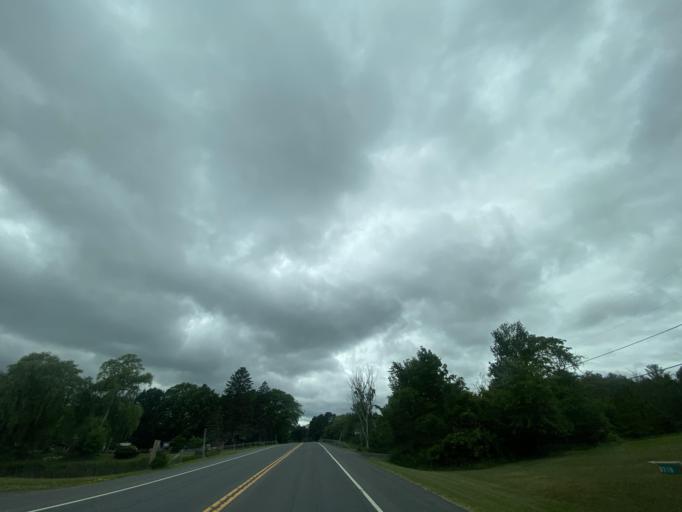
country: US
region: New York
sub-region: Greene County
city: Cairo
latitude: 42.3958
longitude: -73.9778
